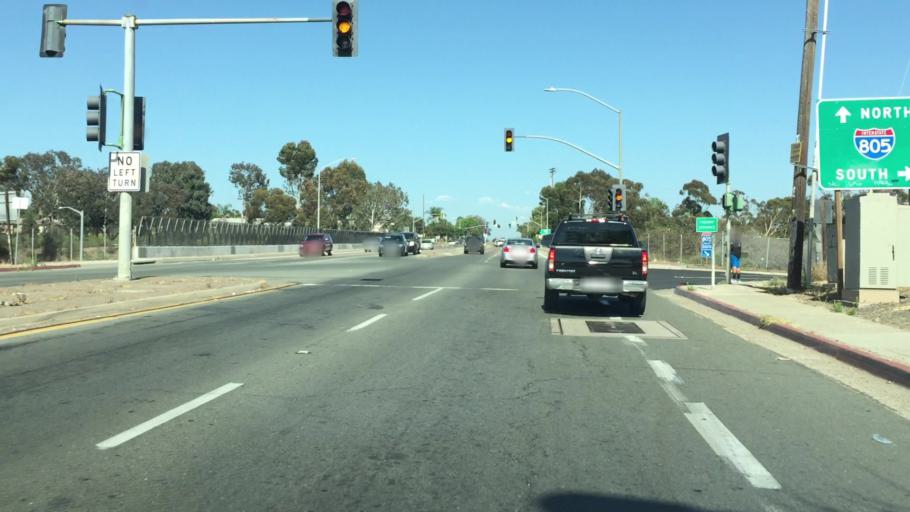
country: US
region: California
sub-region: San Diego County
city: National City
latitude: 32.7114
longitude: -117.1020
